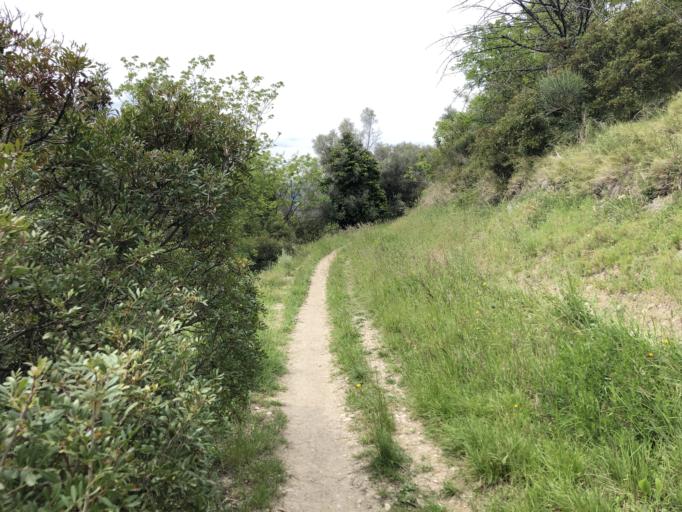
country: FR
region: Provence-Alpes-Cote d'Azur
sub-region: Departement des Alpes-Maritimes
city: Saint-Andre-de-la-Roche
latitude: 43.7222
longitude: 7.2975
